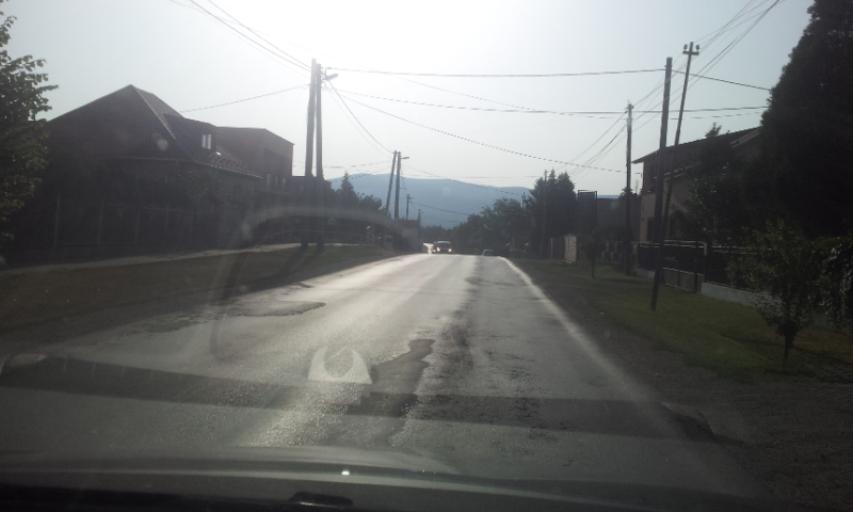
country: SK
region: Kosicky
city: Kosice
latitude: 48.6067
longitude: 21.3157
